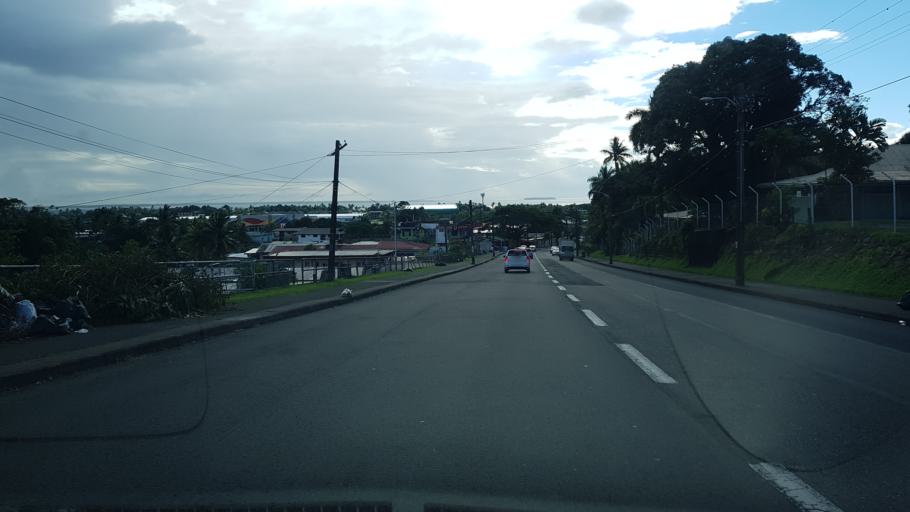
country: FJ
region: Central
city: Suva
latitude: -18.1454
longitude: 178.4428
